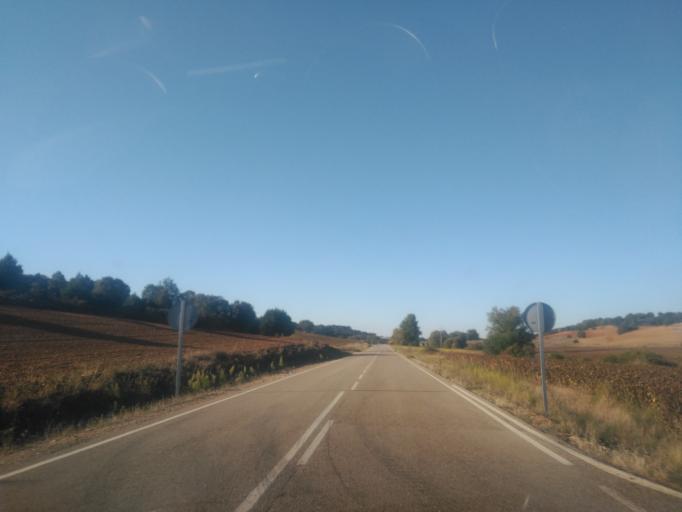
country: ES
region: Castille and Leon
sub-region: Provincia de Soria
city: Alcubilla de Avellaneda
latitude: 41.7491
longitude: -3.2824
